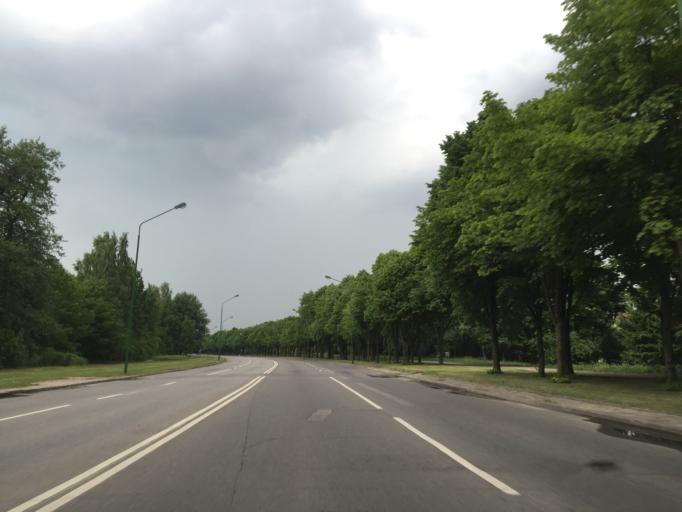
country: LT
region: Klaipedos apskritis
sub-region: Klaipeda
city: Klaipeda
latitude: 55.7346
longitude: 21.1290
